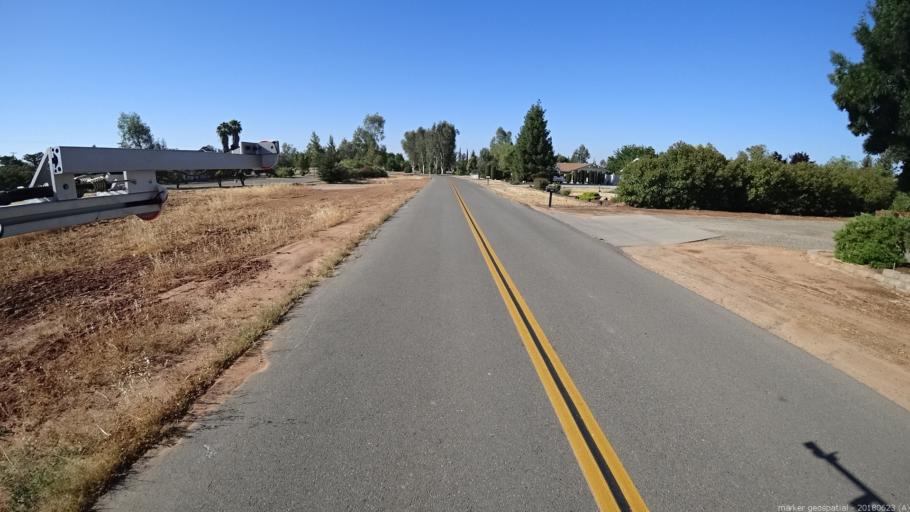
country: US
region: California
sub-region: Madera County
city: Bonadelle Ranchos-Madera Ranchos
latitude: 36.9566
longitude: -119.7961
